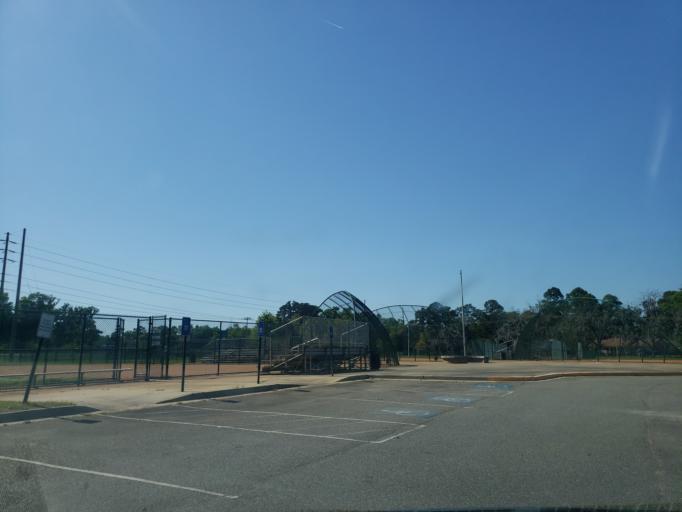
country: US
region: Georgia
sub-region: Chatham County
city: Isle of Hope
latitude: 32.0116
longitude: -81.0811
